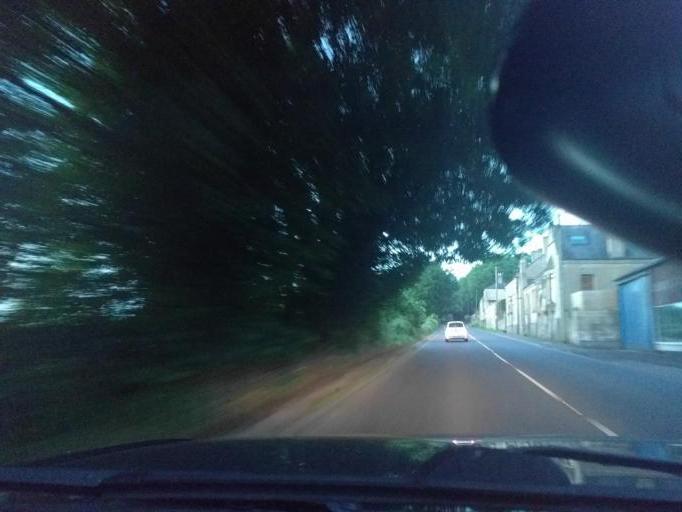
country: GB
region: England
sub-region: Wiltshire
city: Box
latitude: 51.4253
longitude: -2.2368
